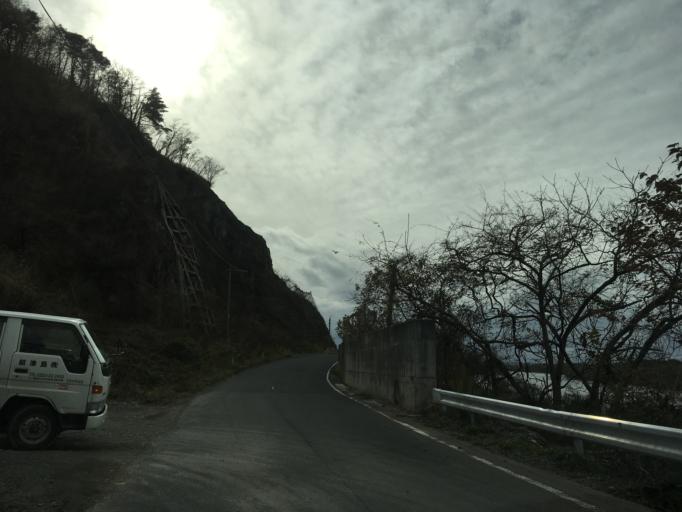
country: JP
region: Iwate
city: Ichinoseki
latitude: 38.7461
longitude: 141.2820
